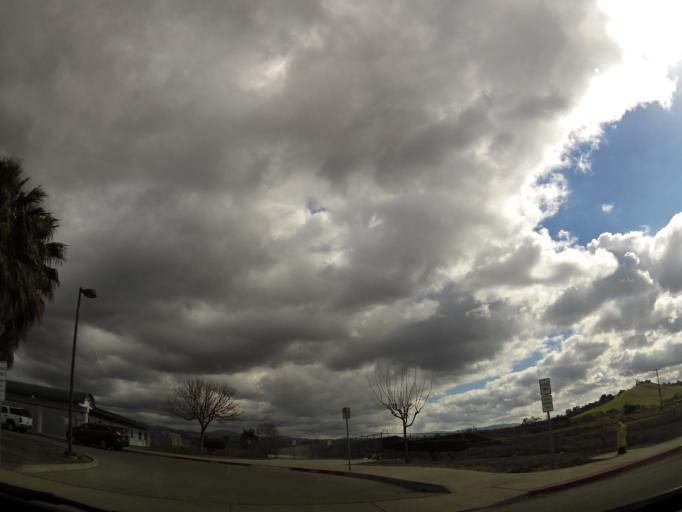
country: US
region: California
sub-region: San Benito County
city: Hollister
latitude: 36.8286
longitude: -121.3933
